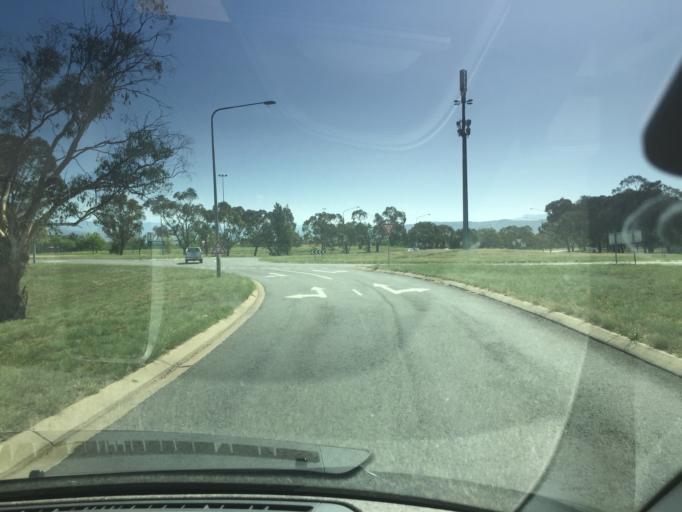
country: AU
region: Australian Capital Territory
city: Macarthur
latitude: -35.4234
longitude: 149.0906
